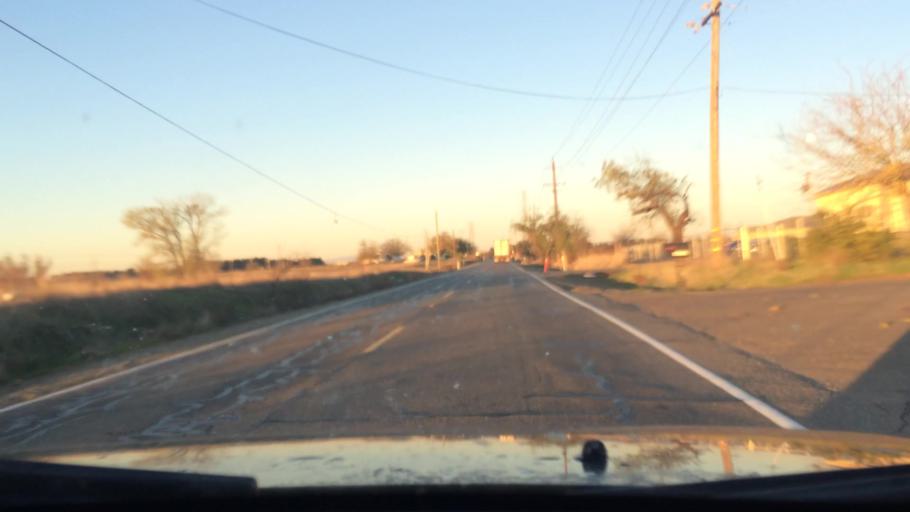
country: US
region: California
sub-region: Sacramento County
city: Vineyard
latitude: 38.5109
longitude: -121.3130
